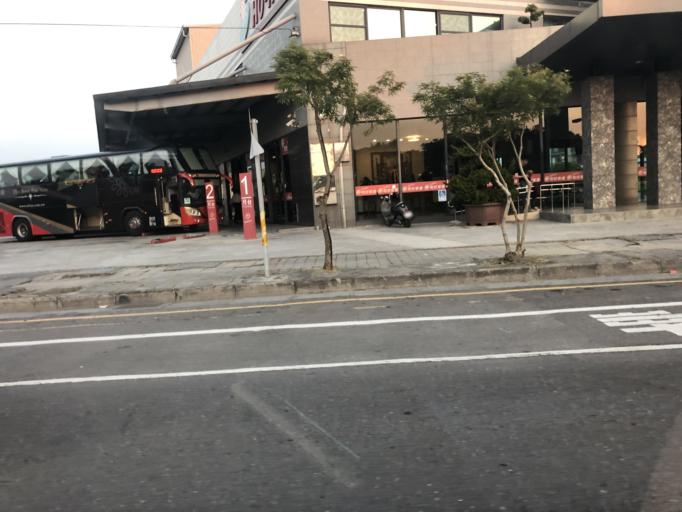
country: TW
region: Taiwan
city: Xinying
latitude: 23.3050
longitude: 120.2931
